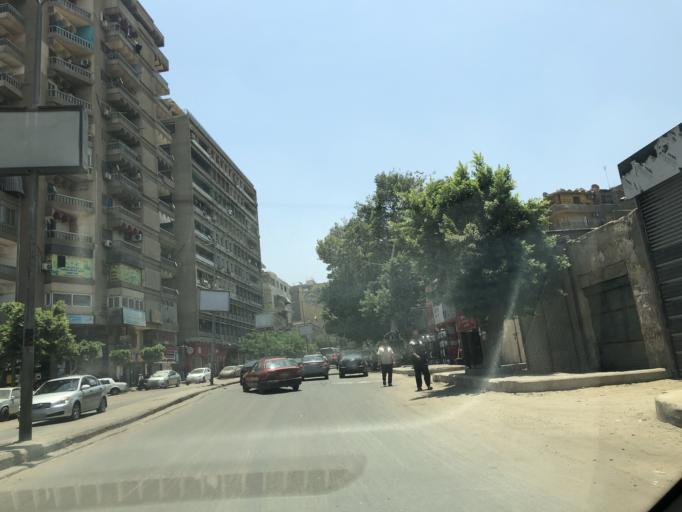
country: EG
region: Muhafazat al Qahirah
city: Cairo
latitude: 30.0653
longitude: 31.2721
